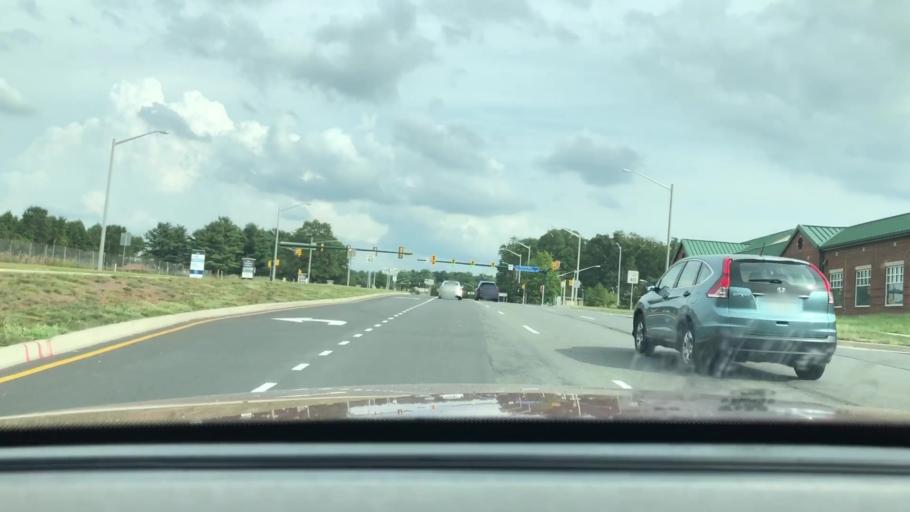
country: US
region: Virginia
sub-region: Fairfax County
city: Chantilly
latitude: 38.8718
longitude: -77.4520
